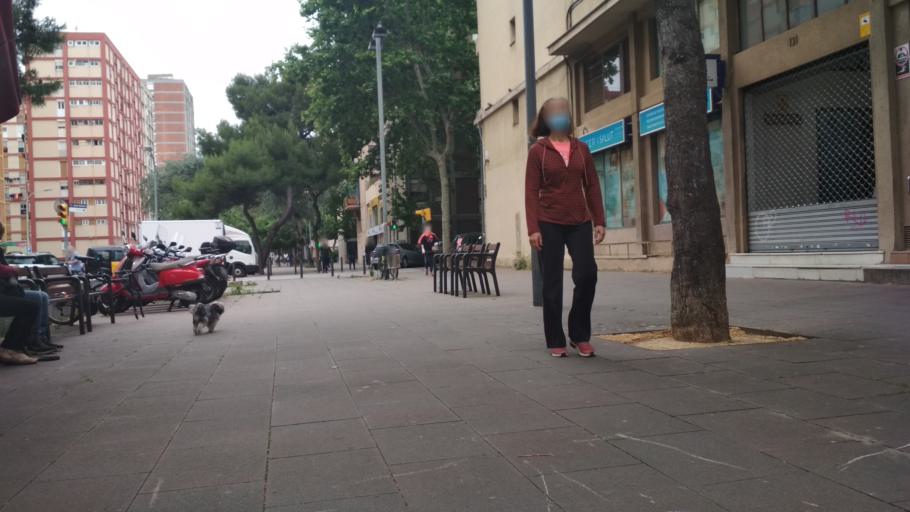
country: ES
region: Catalonia
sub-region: Provincia de Barcelona
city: Sant Marti
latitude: 41.4159
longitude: 2.1981
